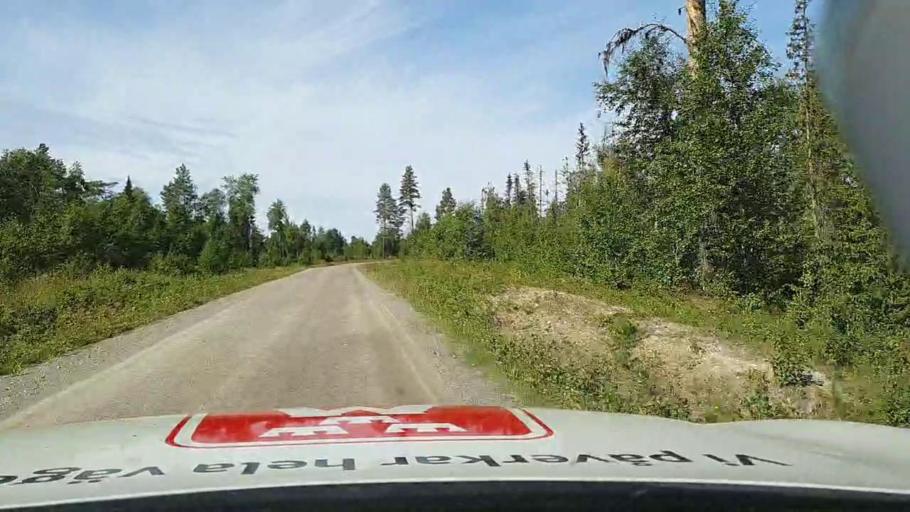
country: SE
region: Jaemtland
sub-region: Stroemsunds Kommun
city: Stroemsund
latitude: 63.7117
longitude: 15.3052
